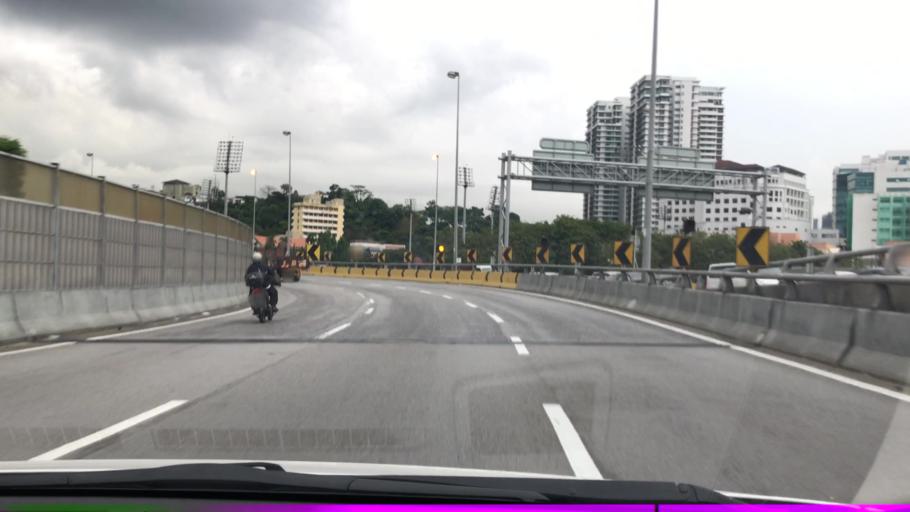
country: MY
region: Kuala Lumpur
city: Kuala Lumpur
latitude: 3.1177
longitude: 101.6633
